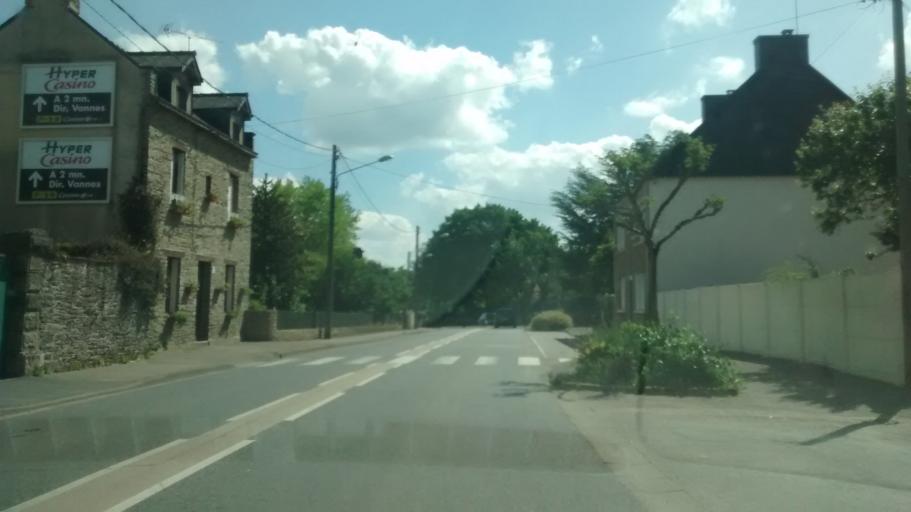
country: FR
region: Brittany
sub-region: Departement du Morbihan
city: Malestroit
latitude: 47.8150
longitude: -2.3754
